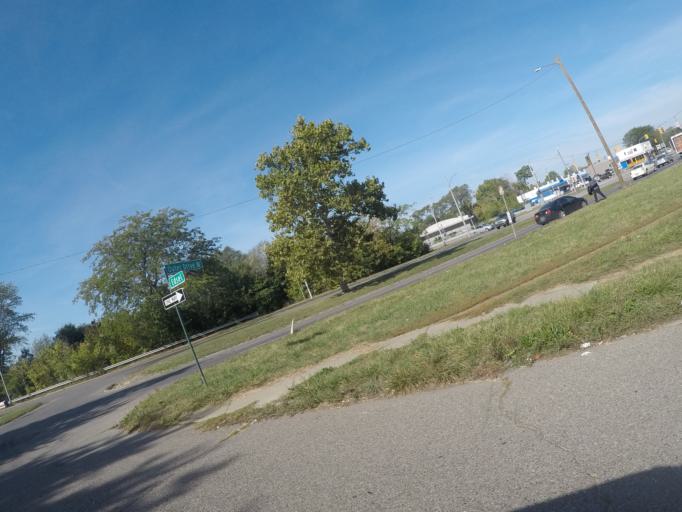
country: US
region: Michigan
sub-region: Wayne County
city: Lincoln Park
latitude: 42.2615
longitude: -83.1663
